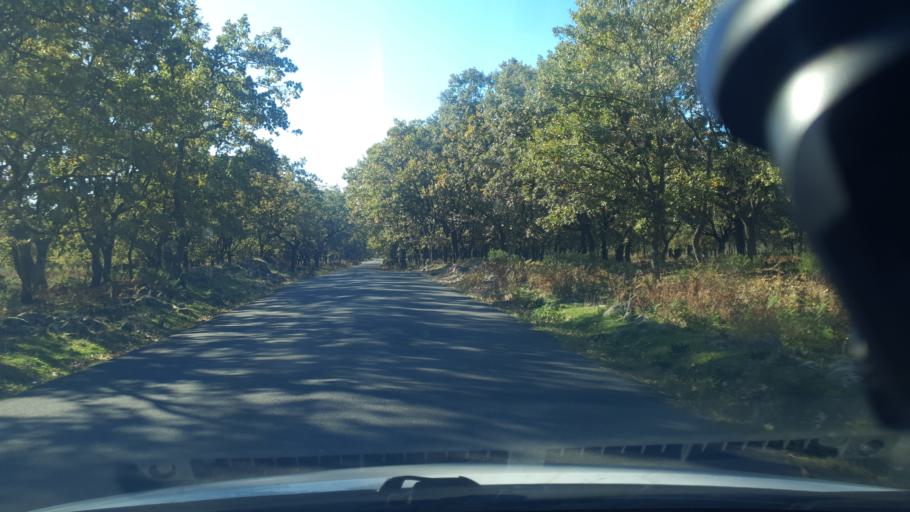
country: ES
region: Castille and Leon
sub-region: Provincia de Avila
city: Candeleda
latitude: 40.1383
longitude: -5.2599
